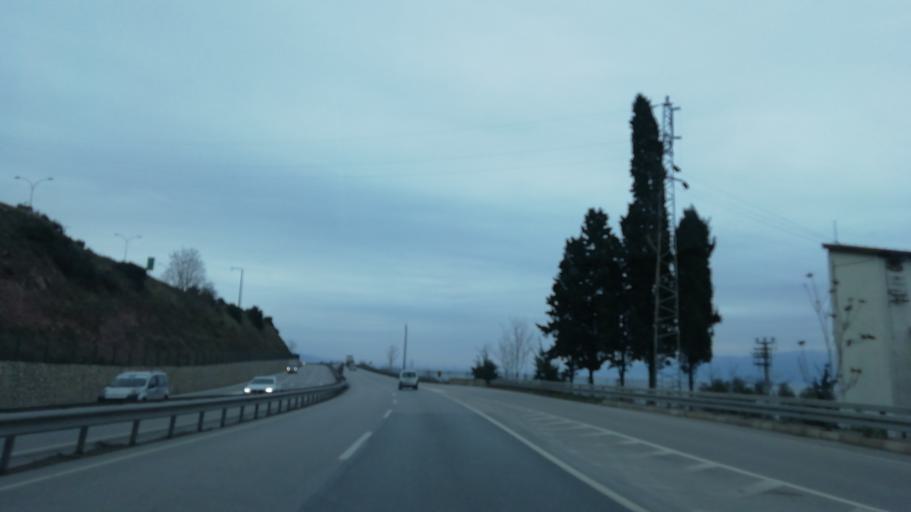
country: TR
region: Kocaeli
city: Tavsancil
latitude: 40.7682
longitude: 29.5725
